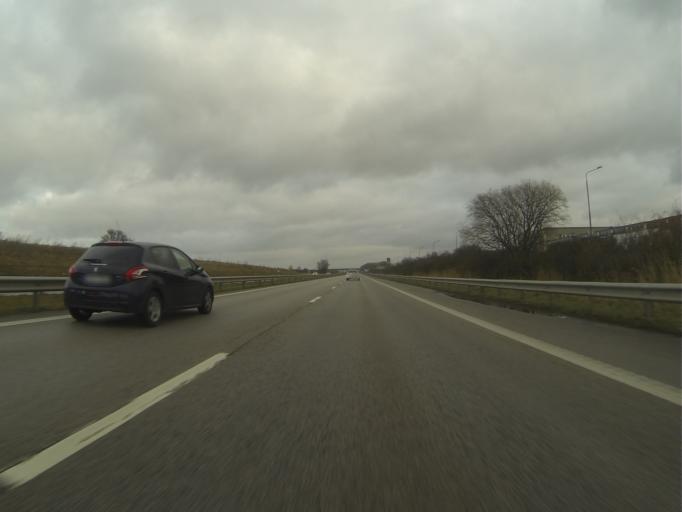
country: SE
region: Skane
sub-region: Burlovs Kommun
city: Arloev
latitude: 55.6462
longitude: 13.0728
